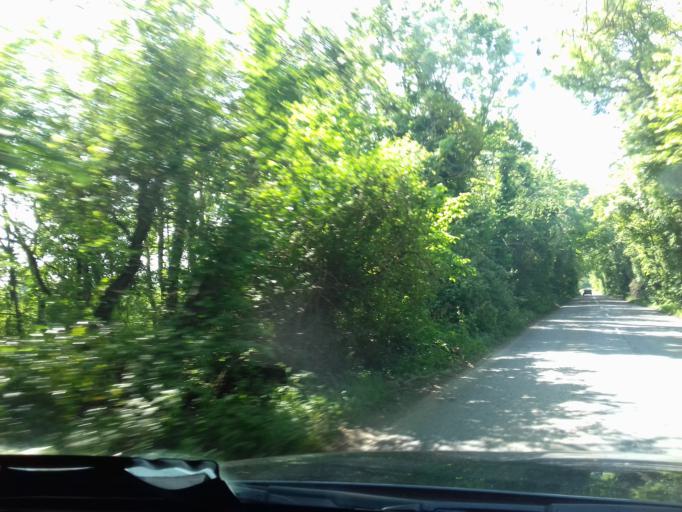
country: IE
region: Leinster
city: Donabate
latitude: 53.4925
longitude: -6.1853
